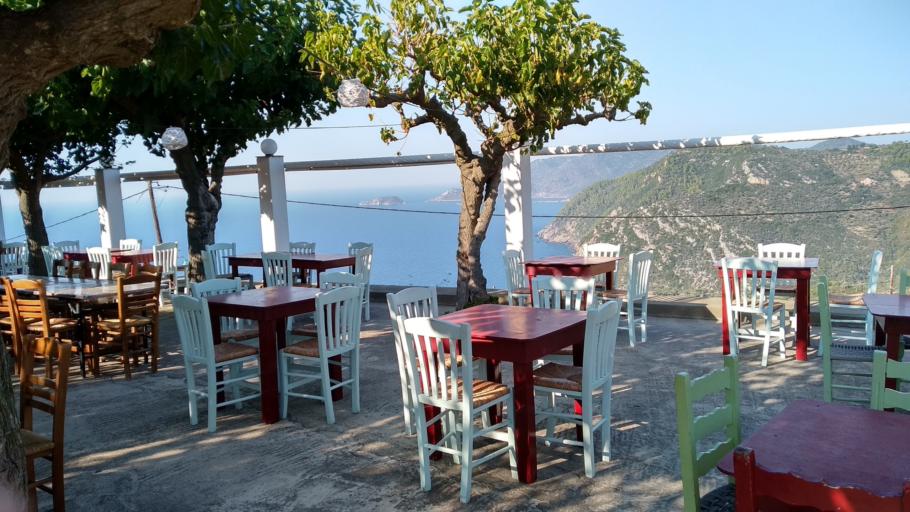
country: GR
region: Thessaly
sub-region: Nomos Magnisias
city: Patitirion
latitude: 39.1504
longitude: 23.8446
